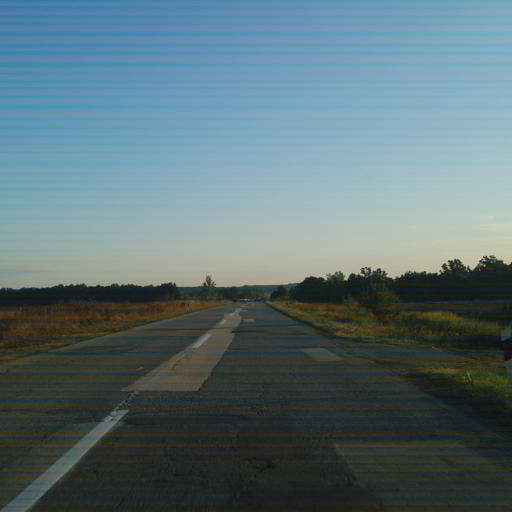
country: RS
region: Central Serbia
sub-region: Borski Okrug
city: Negotin
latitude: 44.1403
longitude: 22.3494
